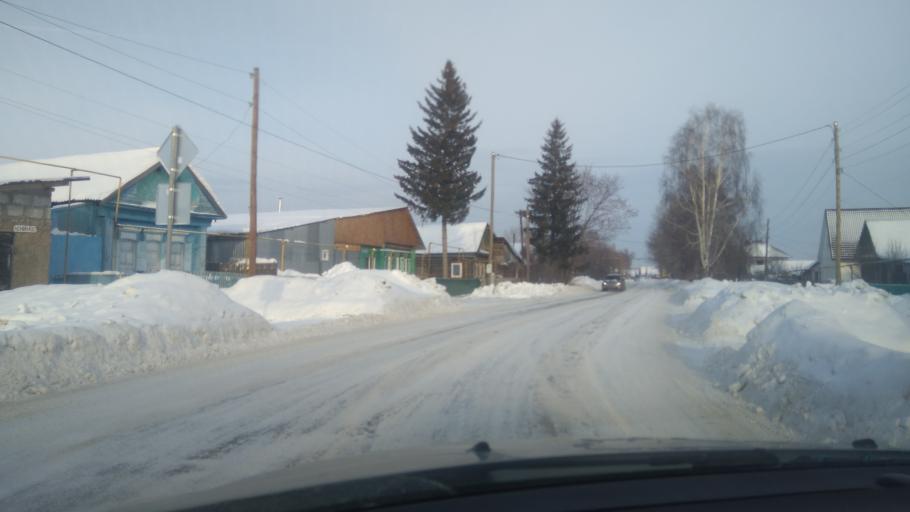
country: RU
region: Sverdlovsk
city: Sukhoy Log
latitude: 56.9066
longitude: 62.0210
